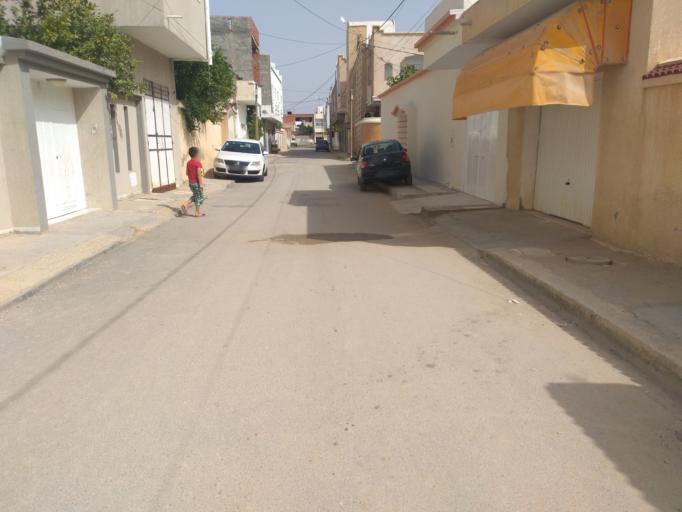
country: TN
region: Al Qayrawan
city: Kairouan
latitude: 35.6651
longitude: 10.0824
